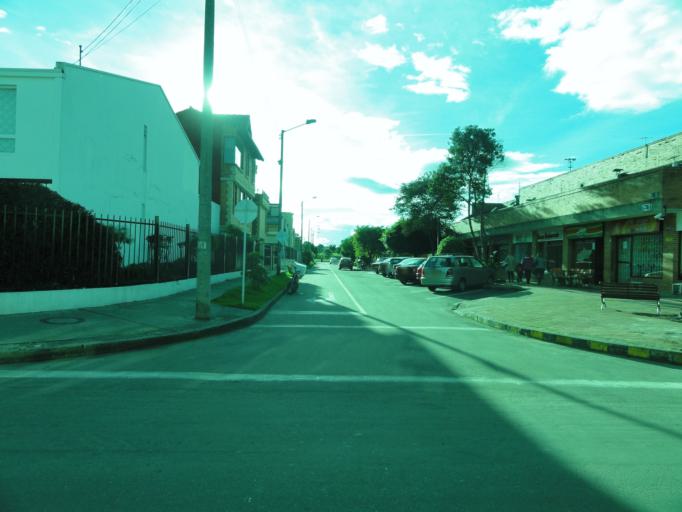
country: CO
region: Bogota D.C.
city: Bogota
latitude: 4.6537
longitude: -74.0865
